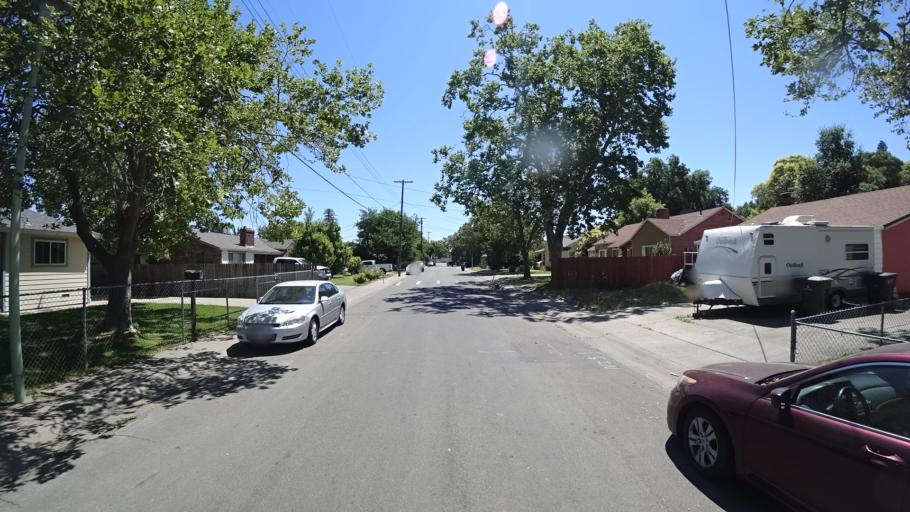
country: US
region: California
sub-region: Sacramento County
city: Parkway
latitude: 38.5351
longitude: -121.4781
